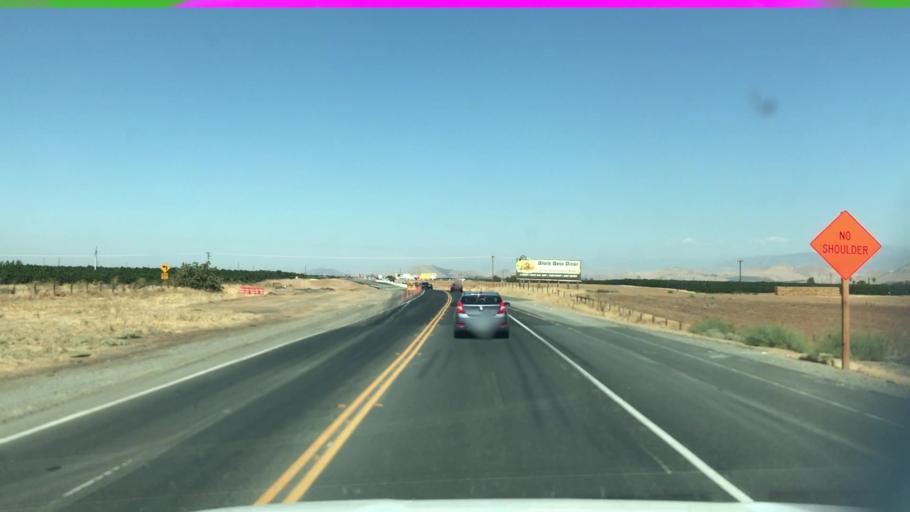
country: US
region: California
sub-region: Tulare County
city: Terra Bella
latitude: 36.0053
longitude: -119.0399
